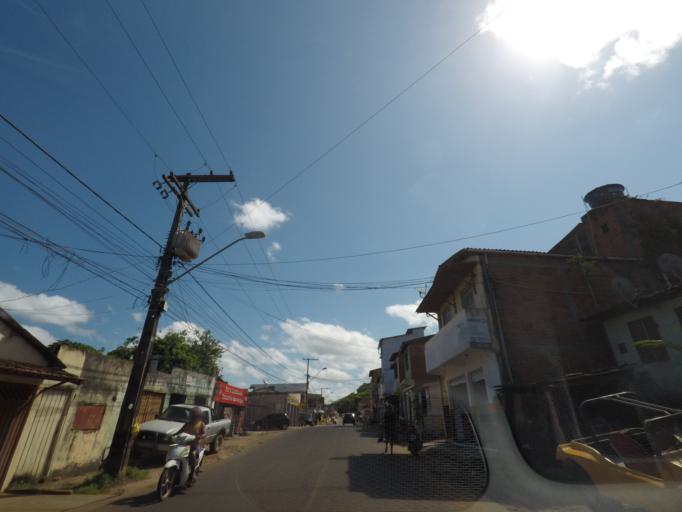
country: BR
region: Bahia
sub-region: Itubera
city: Itubera
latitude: -13.7404
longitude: -39.1500
